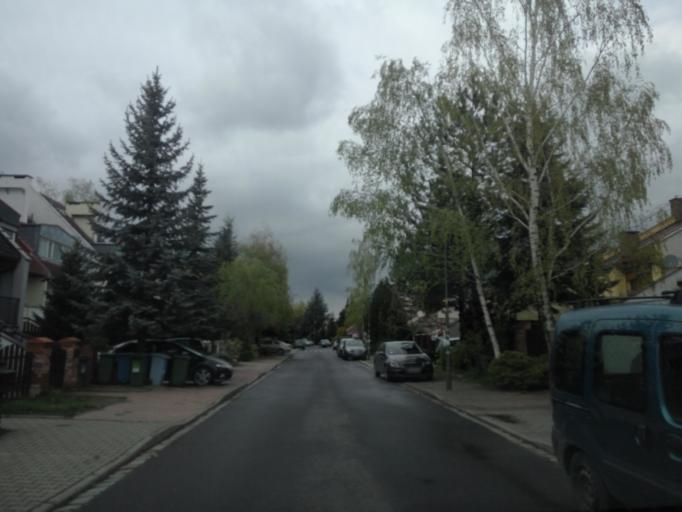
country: PL
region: Lower Silesian Voivodeship
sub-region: Powiat wroclawski
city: Zerniki Wroclawskie
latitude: 51.0592
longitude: 17.0371
